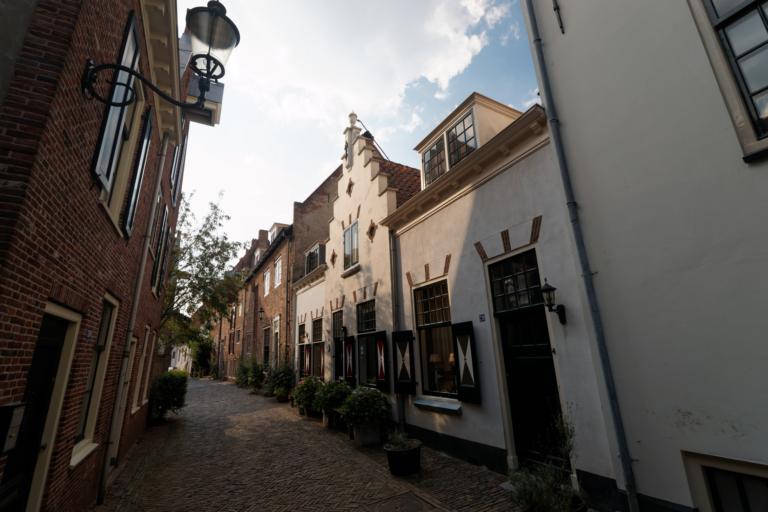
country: NL
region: Utrecht
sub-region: Gemeente Amersfoort
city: Amersfoort
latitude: 52.1579
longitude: 5.3885
